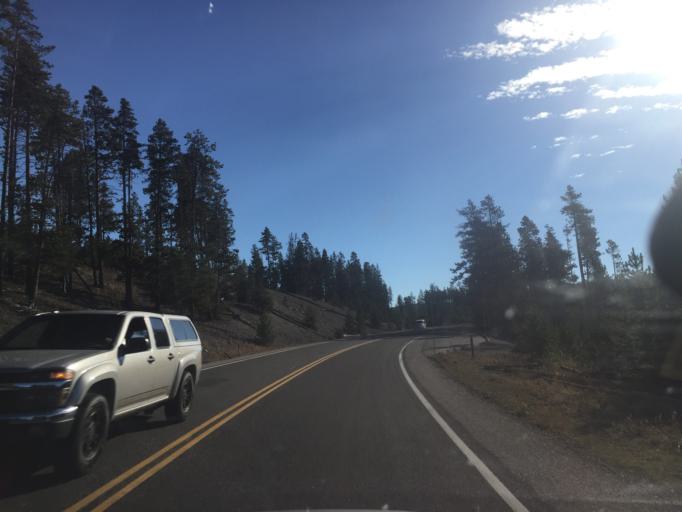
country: US
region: Montana
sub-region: Gallatin County
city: West Yellowstone
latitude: 44.5338
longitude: -110.8244
